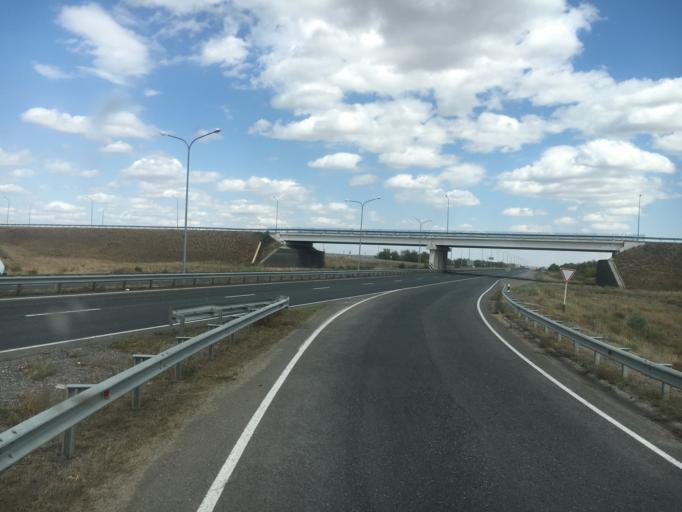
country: KZ
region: Aqtoebe
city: Aqtobe
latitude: 50.2937
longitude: 57.4350
